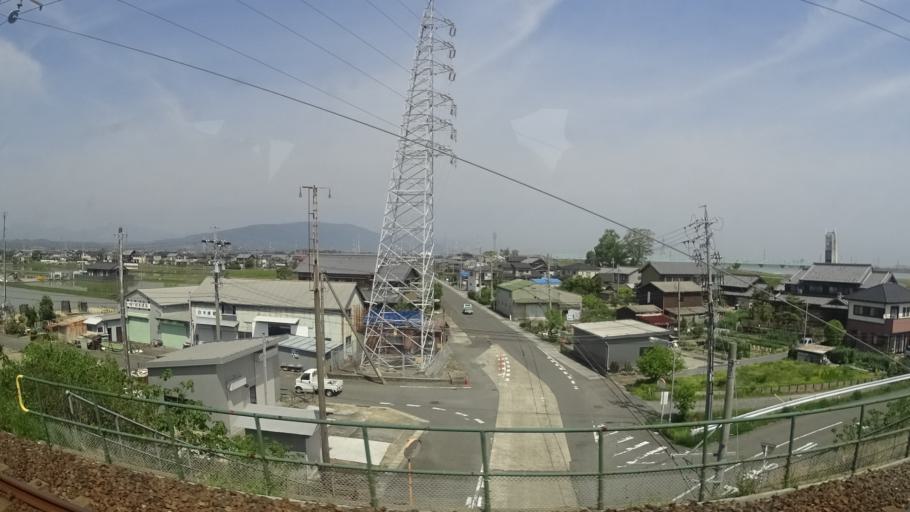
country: JP
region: Aichi
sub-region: Tsushima-shi
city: Tsushima
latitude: 35.1031
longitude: 136.7061
